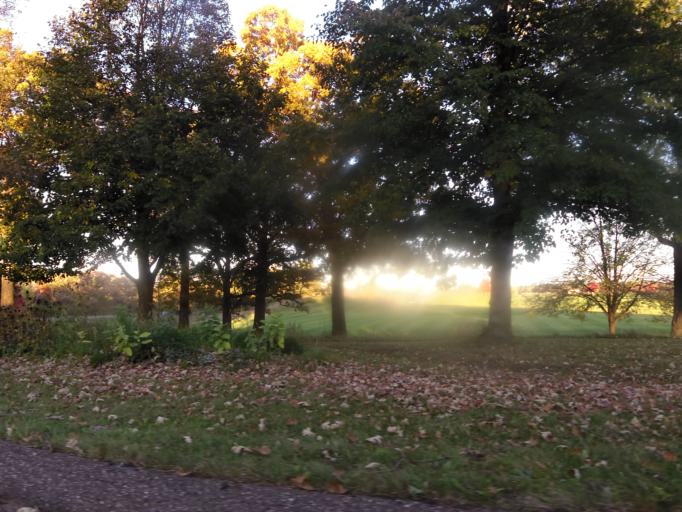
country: US
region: Minnesota
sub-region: Washington County
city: Lake Elmo
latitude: 44.9769
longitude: -92.8743
